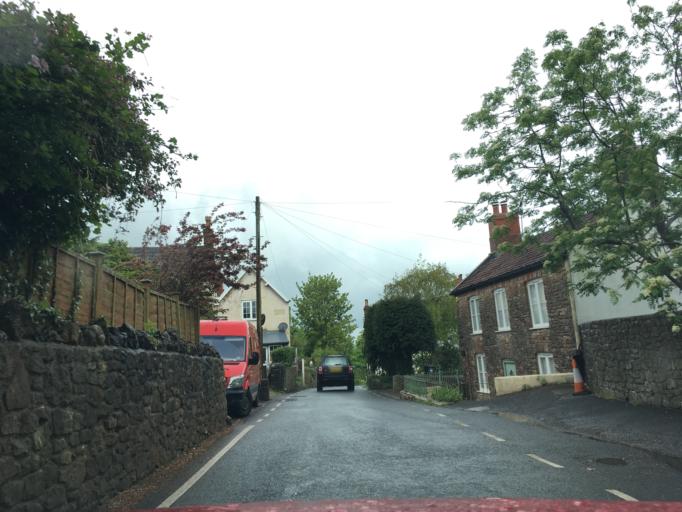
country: GB
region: England
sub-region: North Somerset
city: Blagdon
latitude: 51.3292
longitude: -2.7189
